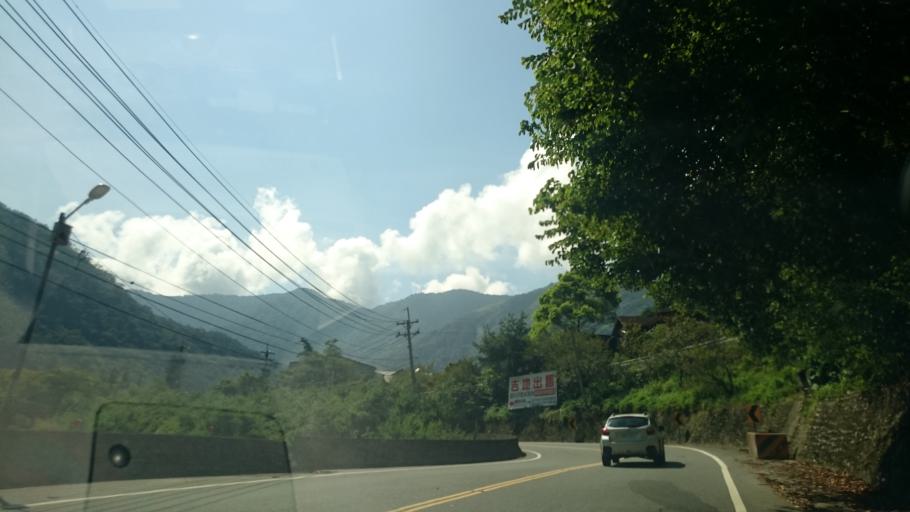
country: TW
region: Taiwan
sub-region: Nantou
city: Puli
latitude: 24.0045
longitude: 121.0640
